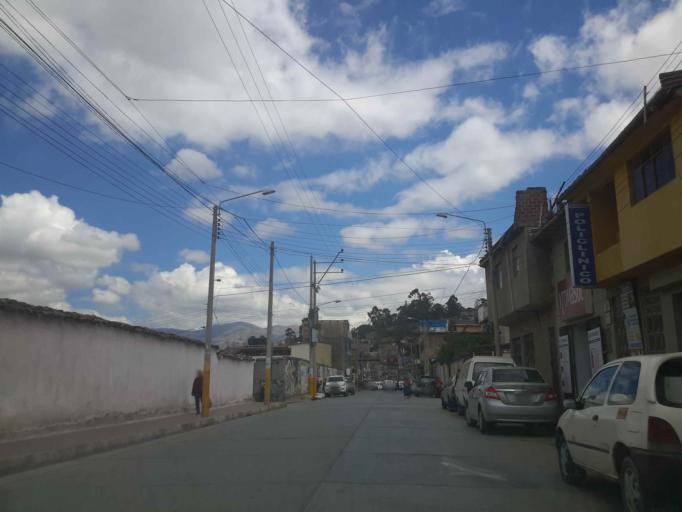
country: PE
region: Apurimac
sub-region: Provincia de Andahuaylas
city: Andahuaylas
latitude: -13.6550
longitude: -73.3861
